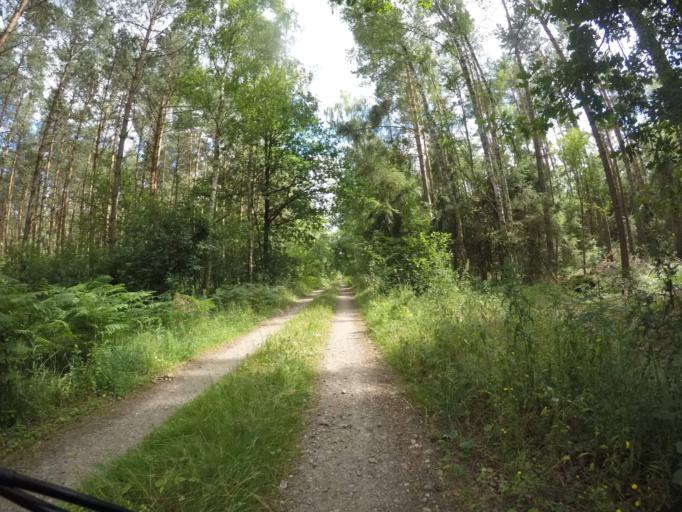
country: DE
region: Mecklenburg-Vorpommern
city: Lubtheen
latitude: 53.2767
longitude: 10.9954
